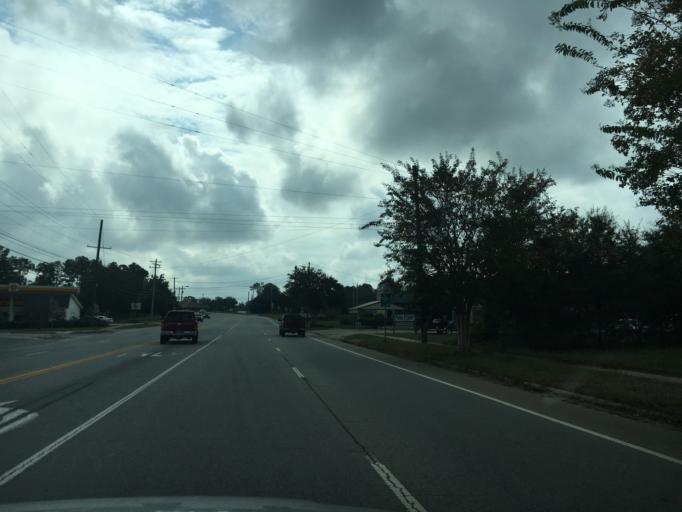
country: US
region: Georgia
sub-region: Elbert County
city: Elberton
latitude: 34.0913
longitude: -82.8473
